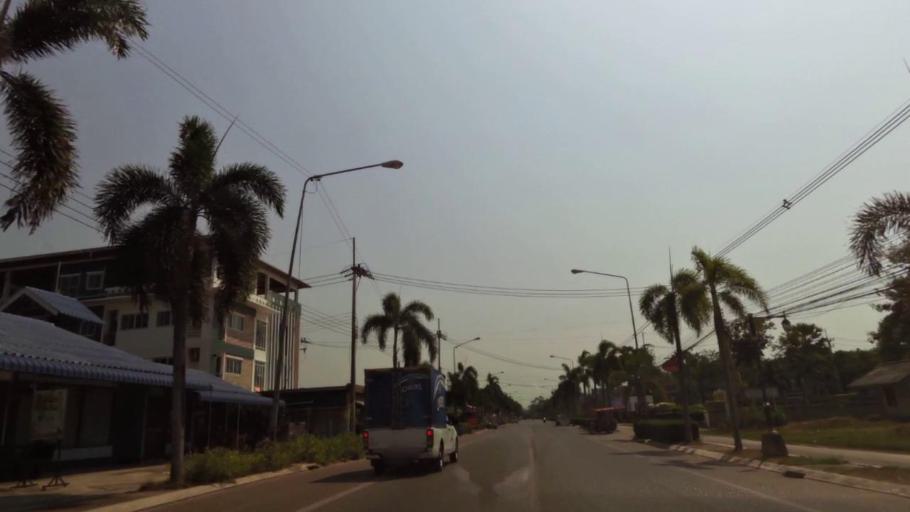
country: TH
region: Chanthaburi
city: Tha Mai
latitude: 12.5542
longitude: 101.9210
